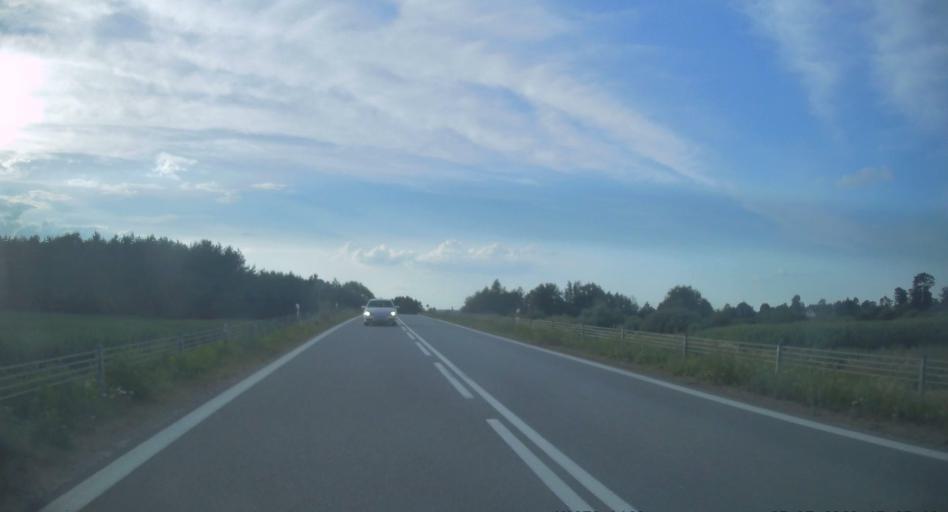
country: PL
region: Lesser Poland Voivodeship
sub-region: Powiat brzeski
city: Szczurowa
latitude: 50.0904
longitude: 20.6253
